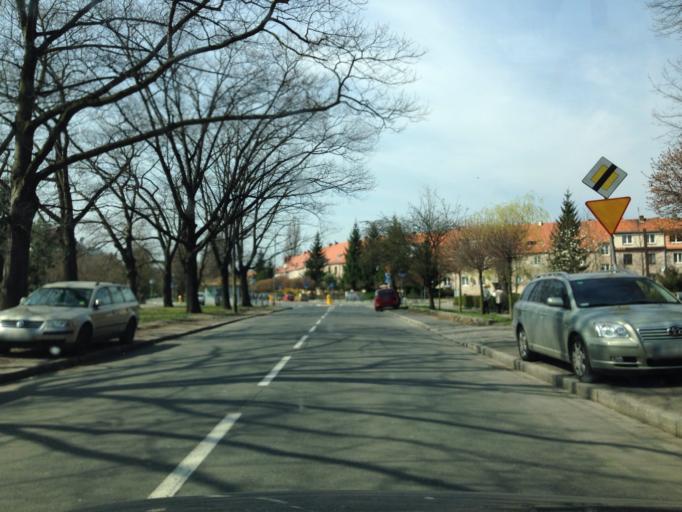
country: PL
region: Lower Silesian Voivodeship
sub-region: Powiat wroclawski
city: Radwanice
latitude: 51.1064
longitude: 17.1072
